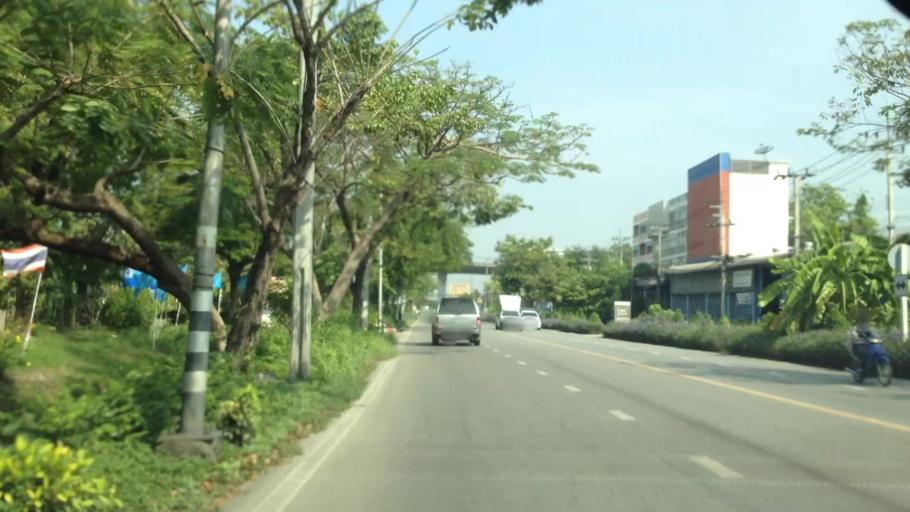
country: TH
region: Bangkok
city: Bang Na
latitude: 13.6622
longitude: 100.6449
